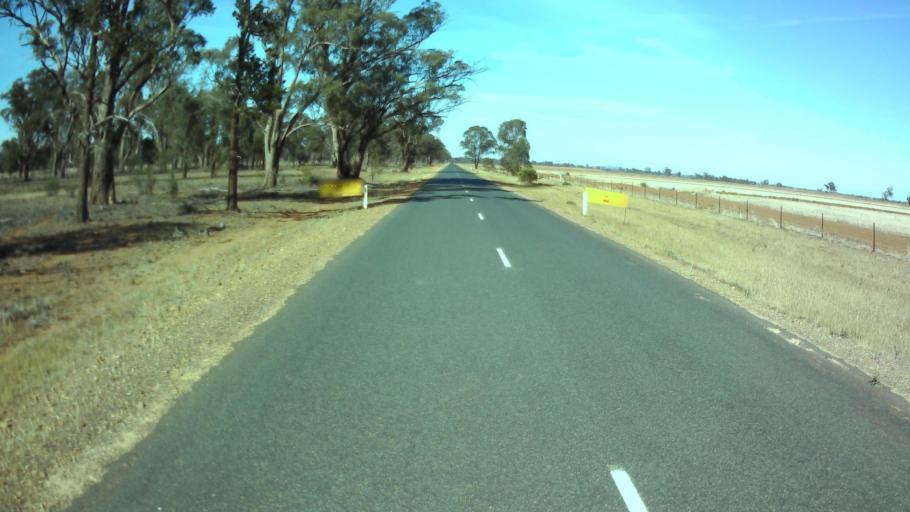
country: AU
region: New South Wales
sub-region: Weddin
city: Grenfell
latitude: -34.1182
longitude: 147.8156
